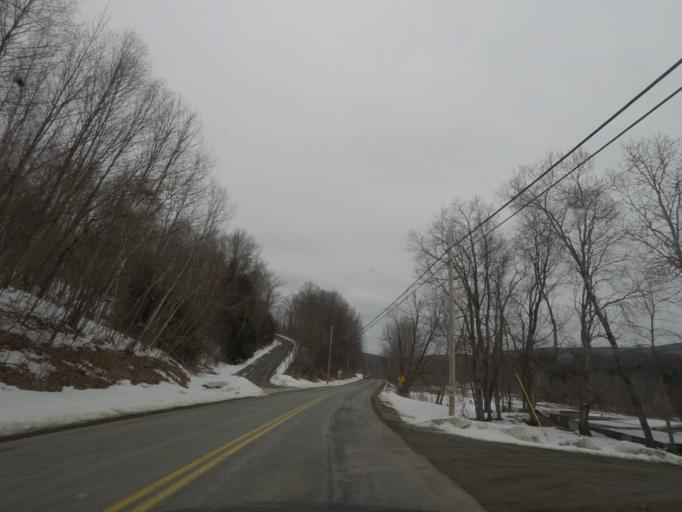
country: US
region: Massachusetts
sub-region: Berkshire County
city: Lanesborough
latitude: 42.5807
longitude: -73.3755
